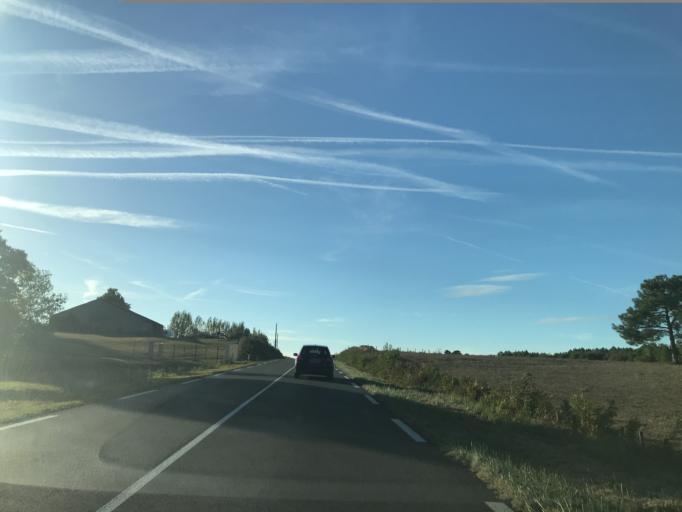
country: FR
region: Poitou-Charentes
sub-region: Departement de la Charente-Maritime
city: Montguyon
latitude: 45.2080
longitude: -0.1619
